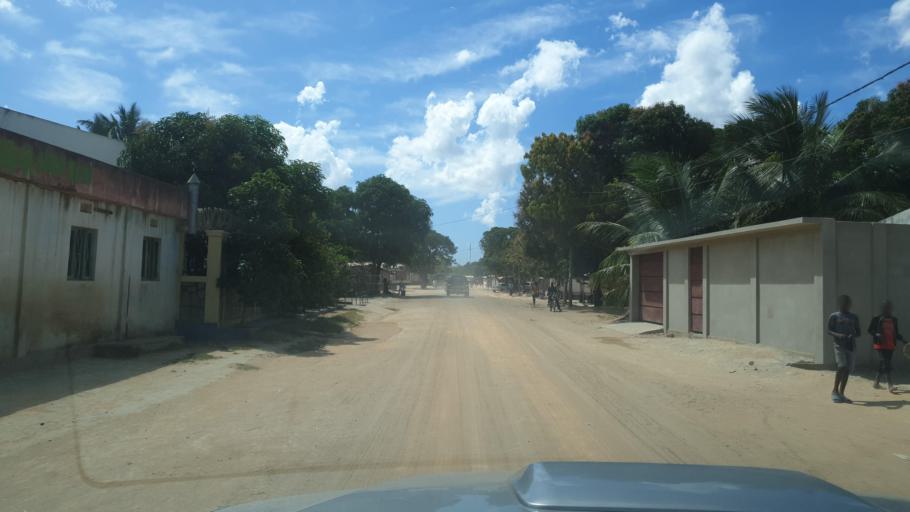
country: MZ
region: Nampula
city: Nacala
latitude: -14.5685
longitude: 40.6960
